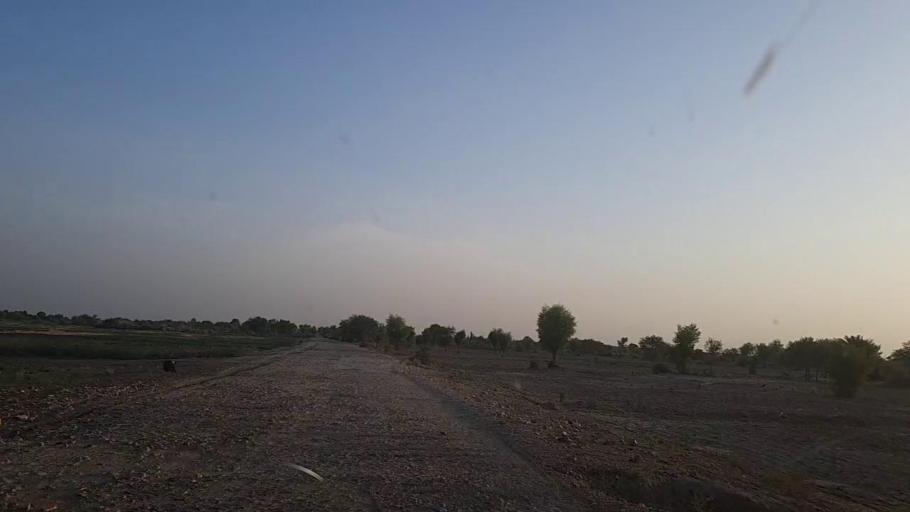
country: PK
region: Sindh
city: Khanpur
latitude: 27.6086
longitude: 69.4361
